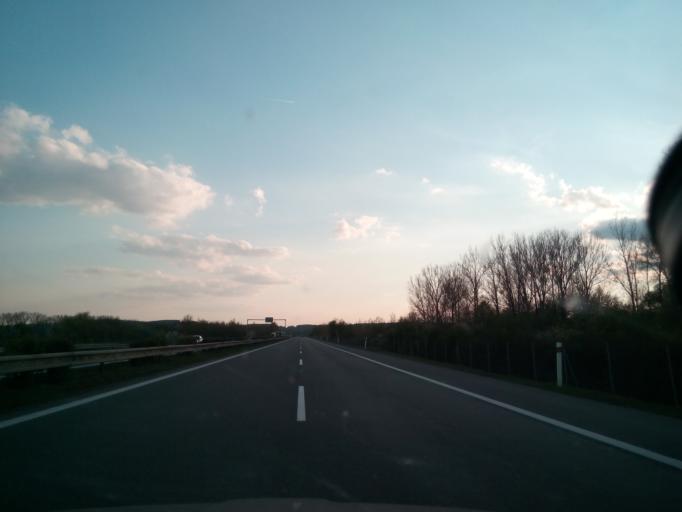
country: SK
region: Nitriansky
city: Nemsova
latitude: 48.9508
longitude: 18.1130
